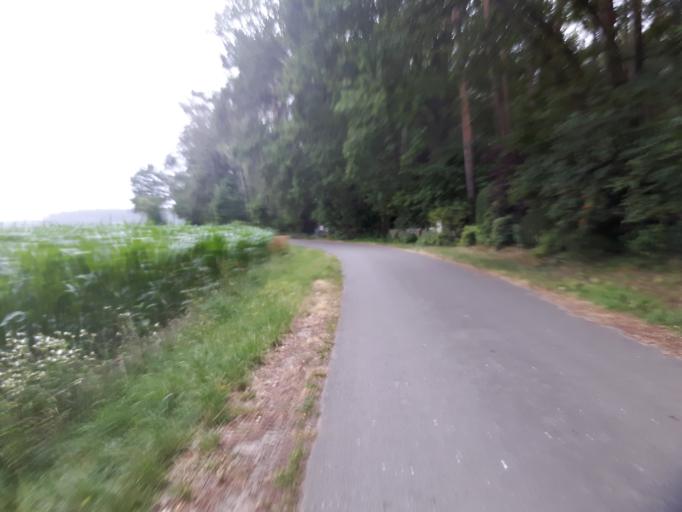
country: DE
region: Lower Saxony
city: Garstedt
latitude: 53.2933
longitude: 10.1896
